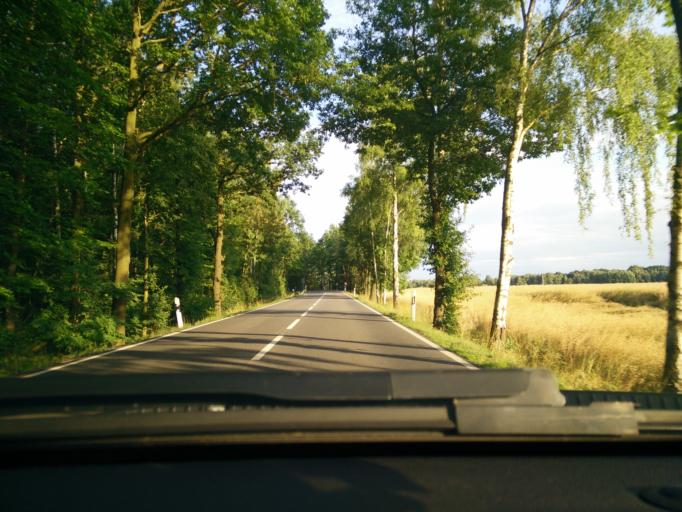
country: DE
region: Saxony
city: Konigsfeld
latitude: 51.0737
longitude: 12.7231
